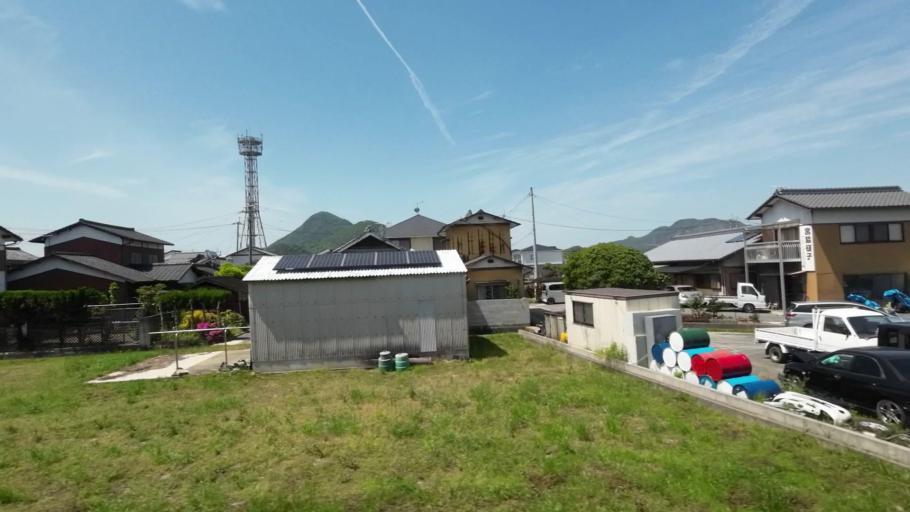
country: JP
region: Kagawa
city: Marugame
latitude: 34.2364
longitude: 133.7855
